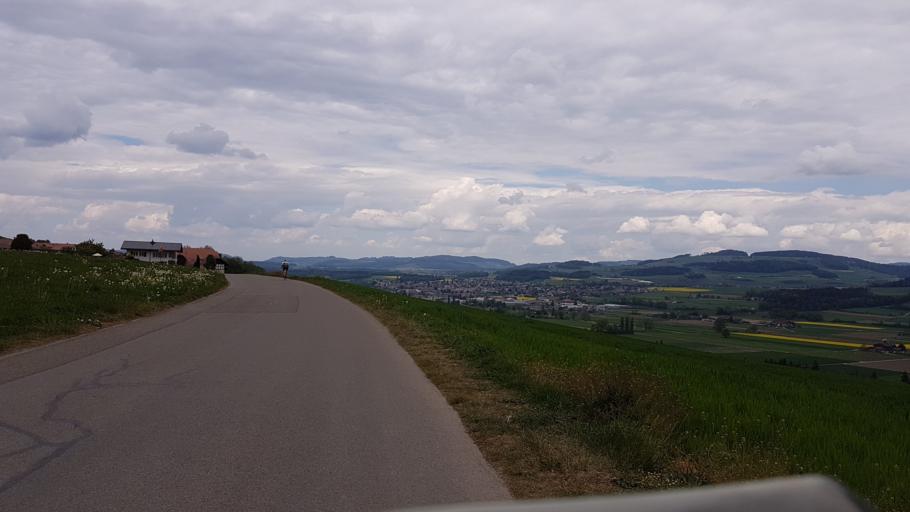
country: CH
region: Bern
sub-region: Bern-Mittelland District
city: Niederwichtrach
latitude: 46.8469
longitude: 7.5510
